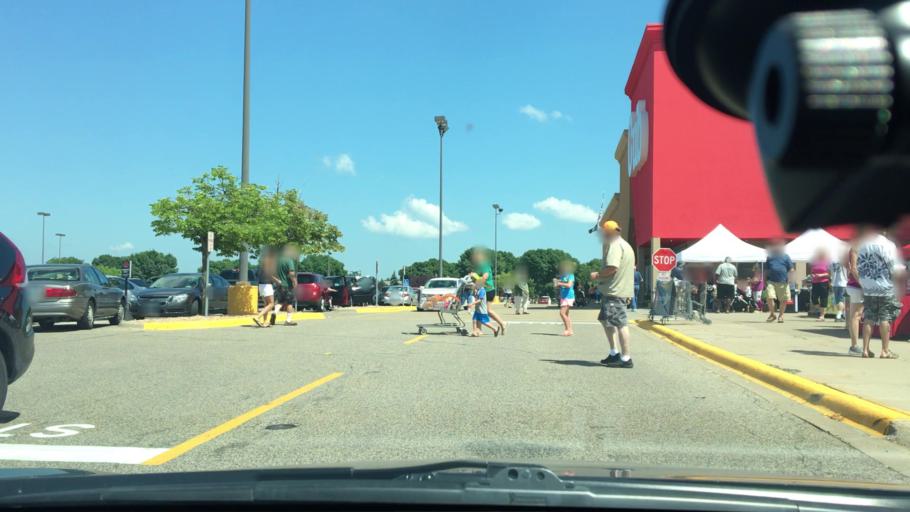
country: US
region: Minnesota
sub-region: Hennepin County
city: Maple Grove
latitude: 45.1020
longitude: -93.4484
